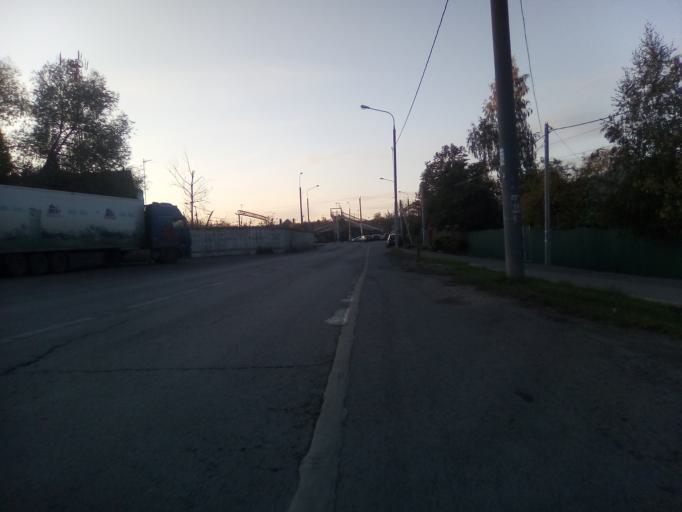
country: RU
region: Moskovskaya
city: Kokoshkino
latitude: 55.6062
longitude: 37.1877
